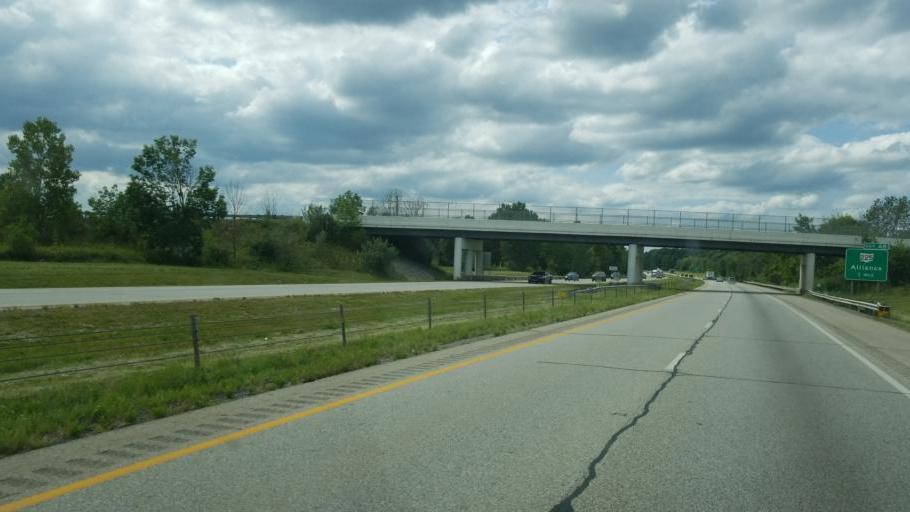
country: US
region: Ohio
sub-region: Mahoning County
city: Craig Beach
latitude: 41.1039
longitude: -81.0309
